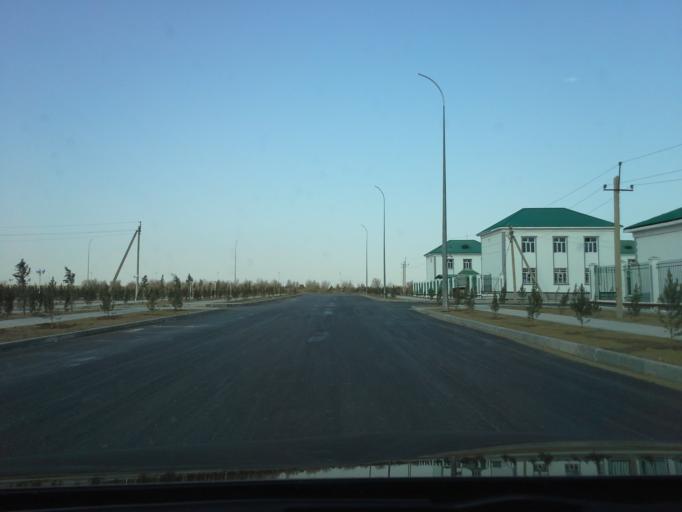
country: TM
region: Ahal
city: Abadan
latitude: 38.0989
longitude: 58.3122
